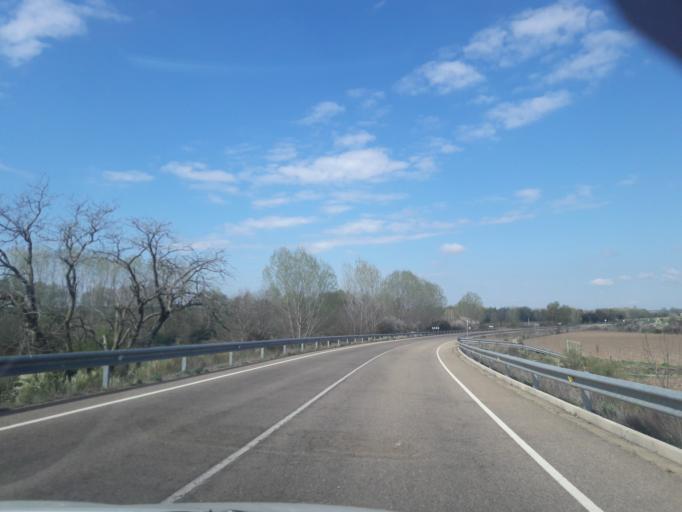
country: ES
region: Castille and Leon
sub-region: Provincia de Salamanca
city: Ciudad Rodrigo
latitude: 40.5749
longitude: -6.4963
